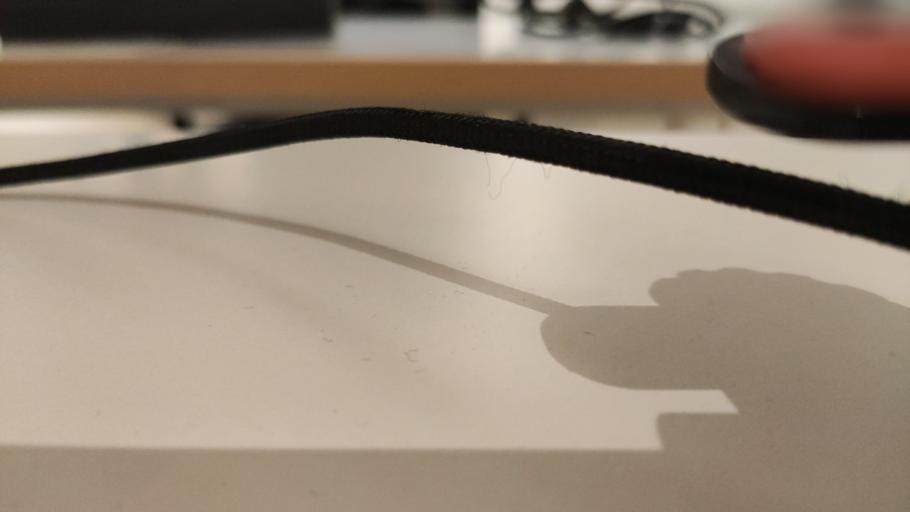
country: RU
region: Moskovskaya
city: Dorokhovo
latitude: 55.5009
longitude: 36.3469
